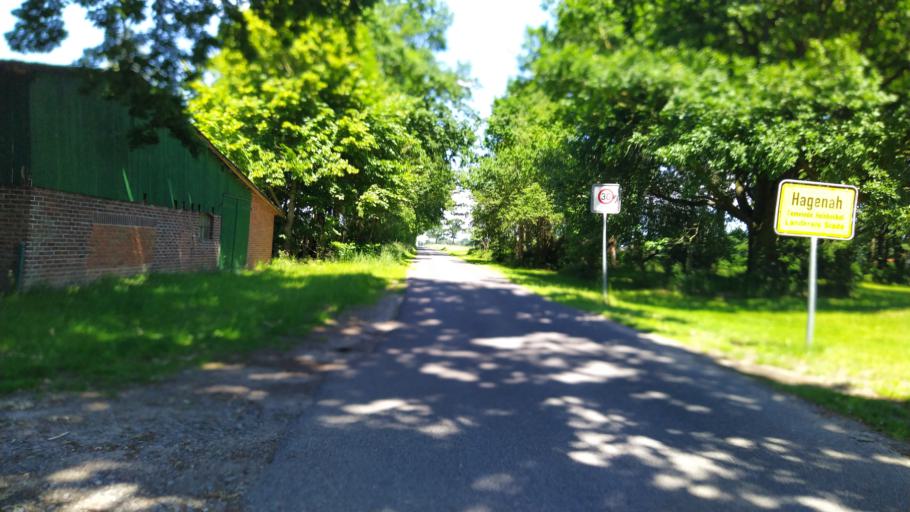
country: DE
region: Lower Saxony
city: Heinbockel
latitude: 53.5438
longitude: 9.3088
